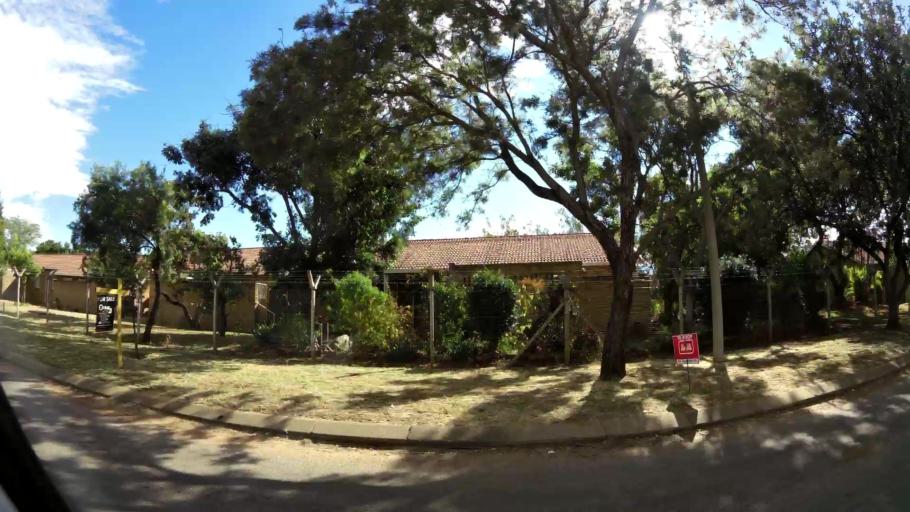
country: ZA
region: Limpopo
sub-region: Waterberg District Municipality
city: Warmbaths
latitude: -24.8734
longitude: 28.2853
